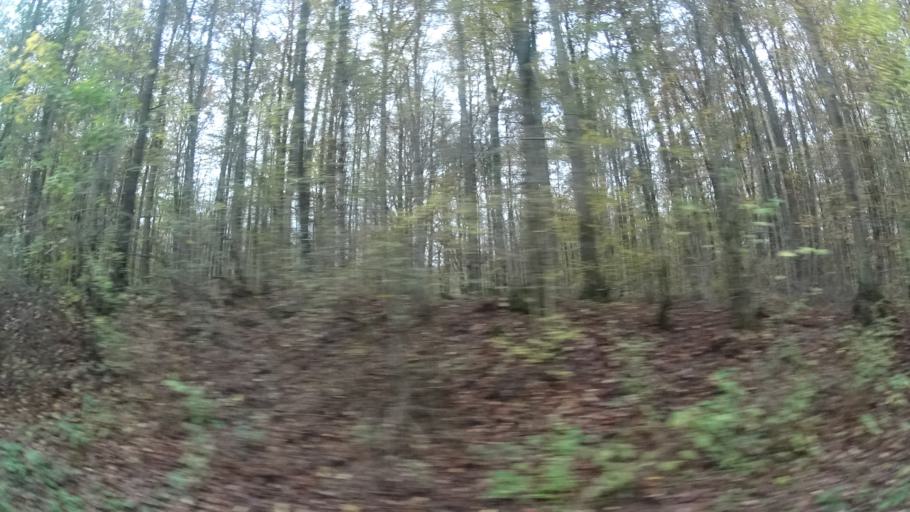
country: DE
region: Thuringia
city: Gleichamberg
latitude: 50.4010
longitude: 10.5942
